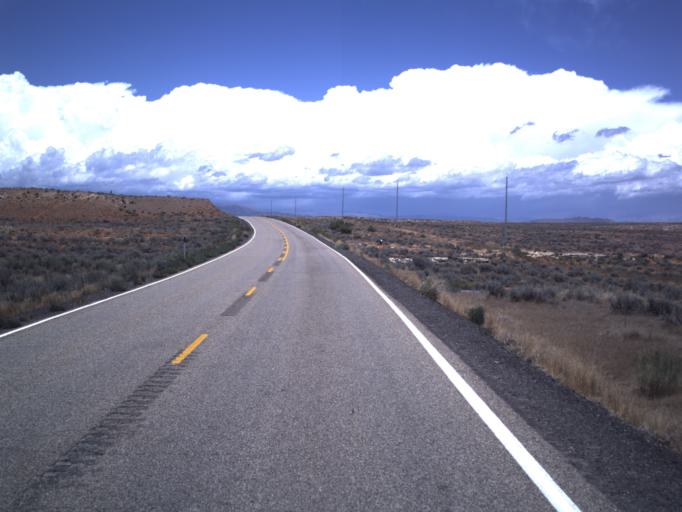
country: US
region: Utah
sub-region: Uintah County
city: Maeser
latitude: 40.2761
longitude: -109.6817
